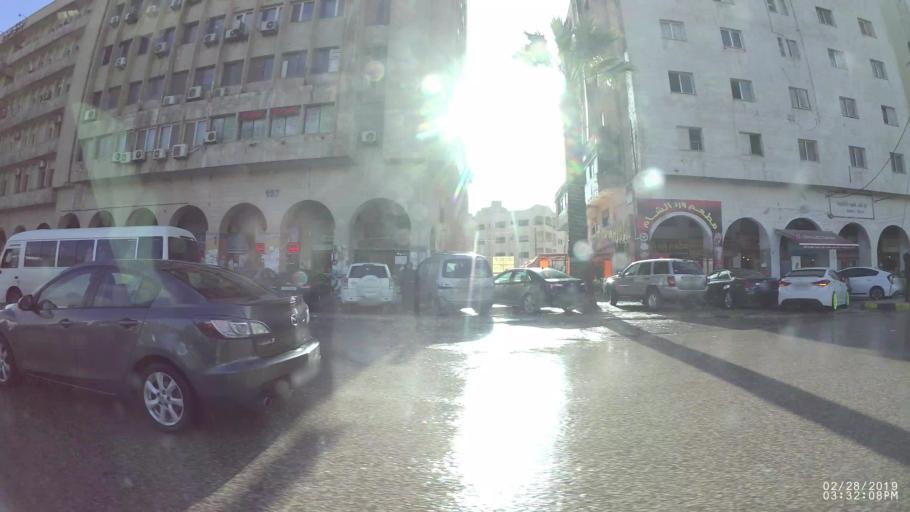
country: JO
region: Amman
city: Al Jubayhah
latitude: 32.0050
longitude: 35.8732
